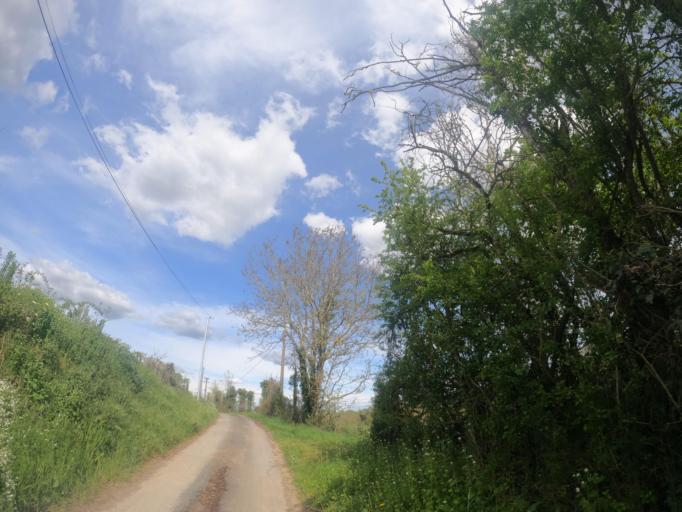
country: FR
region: Poitou-Charentes
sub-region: Departement des Deux-Sevres
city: Saint-Varent
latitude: 46.9181
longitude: -0.1930
